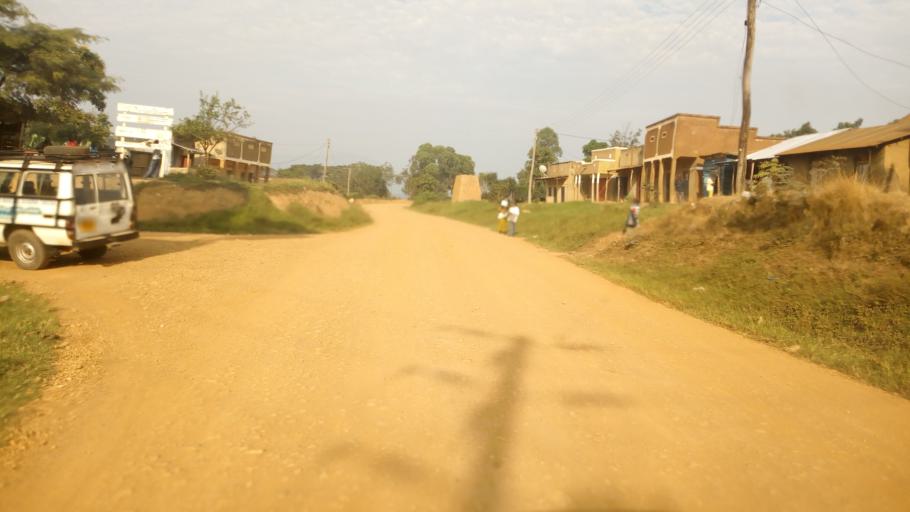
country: UG
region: Western Region
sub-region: Kanungu District
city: Ntungamo
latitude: -0.8359
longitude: 29.6831
